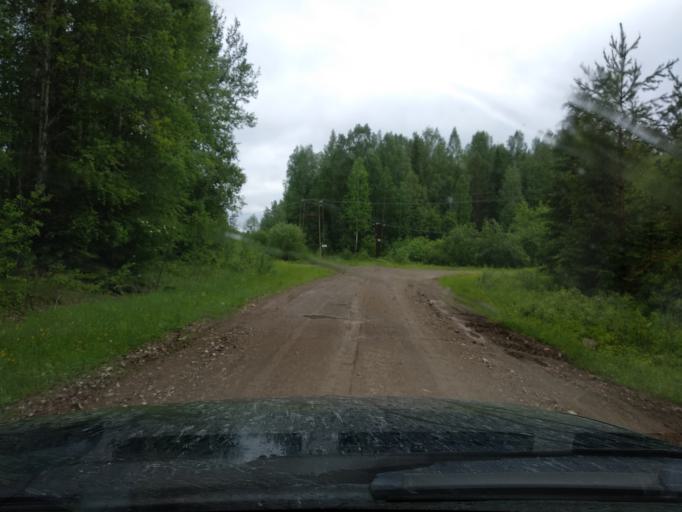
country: RU
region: Sverdlovsk
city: Karpinsk
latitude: 59.4421
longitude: 59.9726
